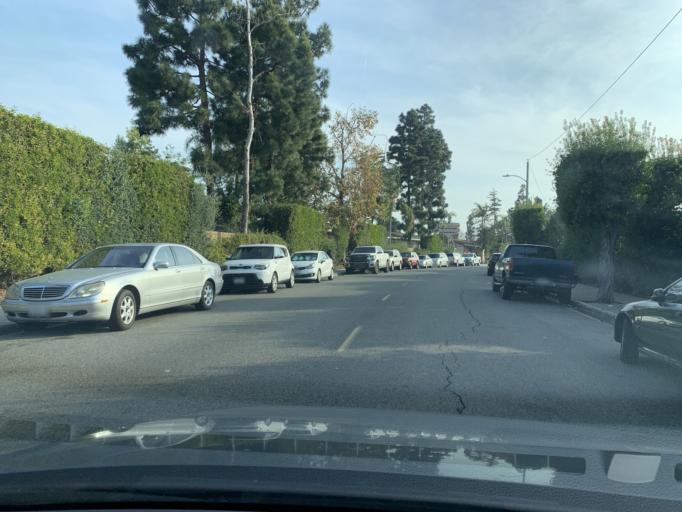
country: US
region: California
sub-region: Orange County
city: Westminster
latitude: 33.7730
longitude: -118.0267
